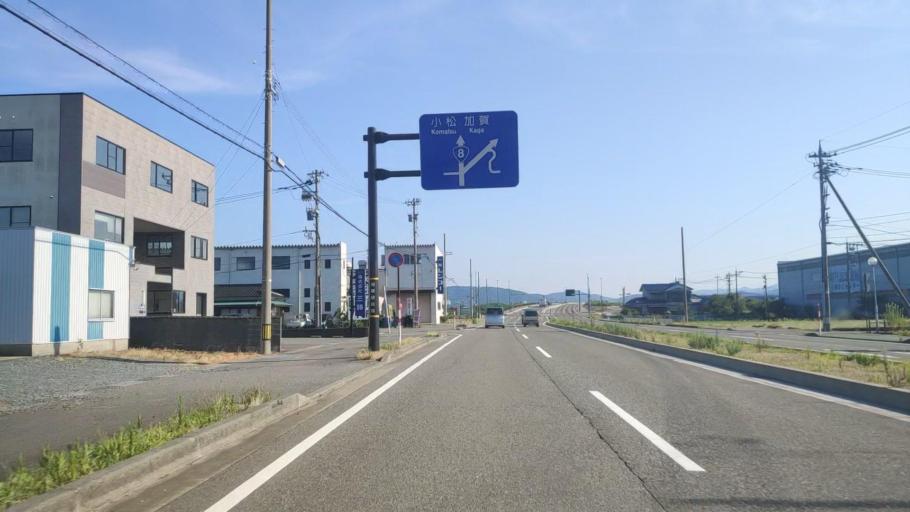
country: JP
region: Fukui
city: Maruoka
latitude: 36.1678
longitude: 136.2633
